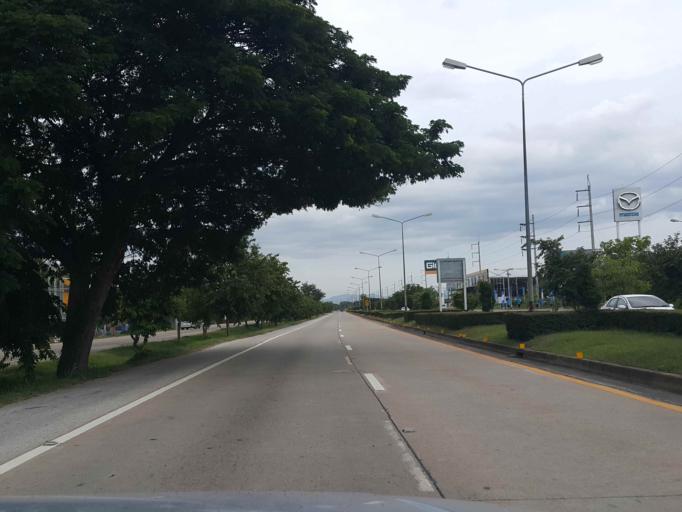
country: TH
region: Lampang
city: Lampang
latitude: 18.2844
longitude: 99.4489
